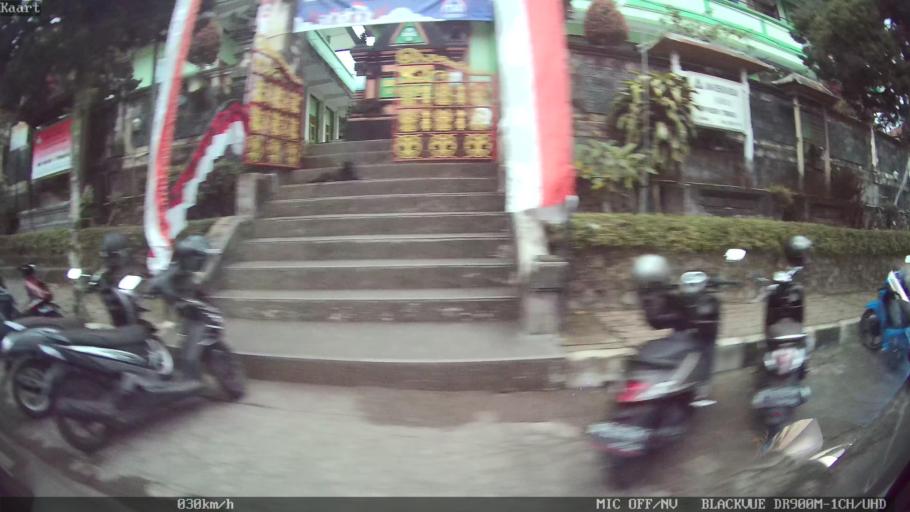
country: ID
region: Bali
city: Bangli
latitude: -8.4527
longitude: 115.3847
